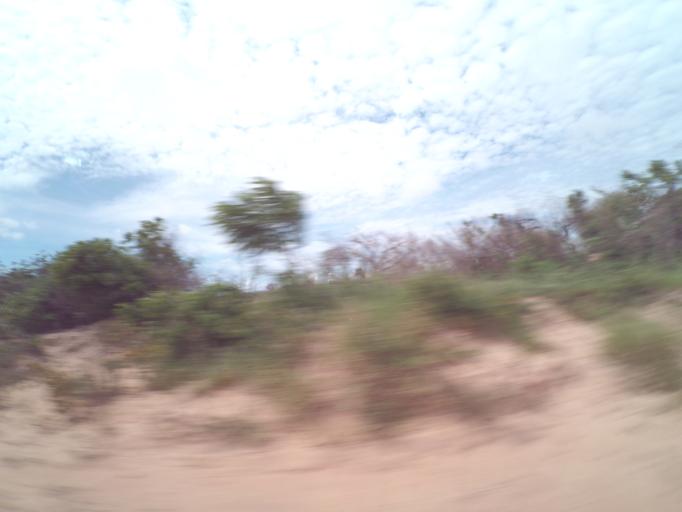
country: BO
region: Santa Cruz
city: Santa Cruz de la Sierra
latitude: -17.8987
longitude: -63.1752
